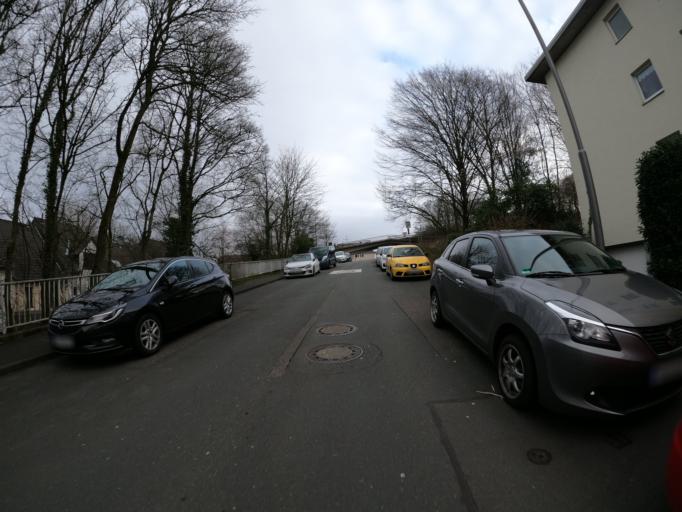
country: DE
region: North Rhine-Westphalia
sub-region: Regierungsbezirk Dusseldorf
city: Wuppertal
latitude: 51.2478
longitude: 7.1464
